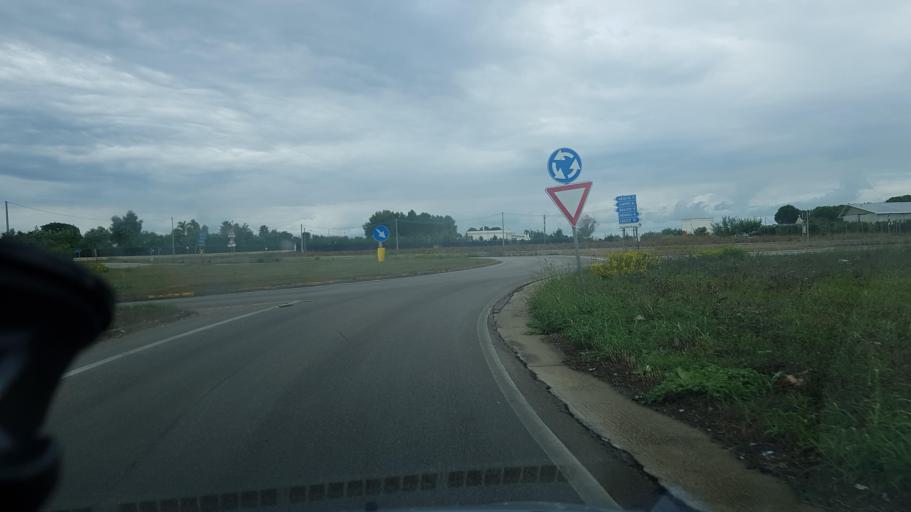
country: IT
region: Apulia
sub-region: Provincia di Lecce
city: Campi Salentina
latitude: 40.3626
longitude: 18.0096
